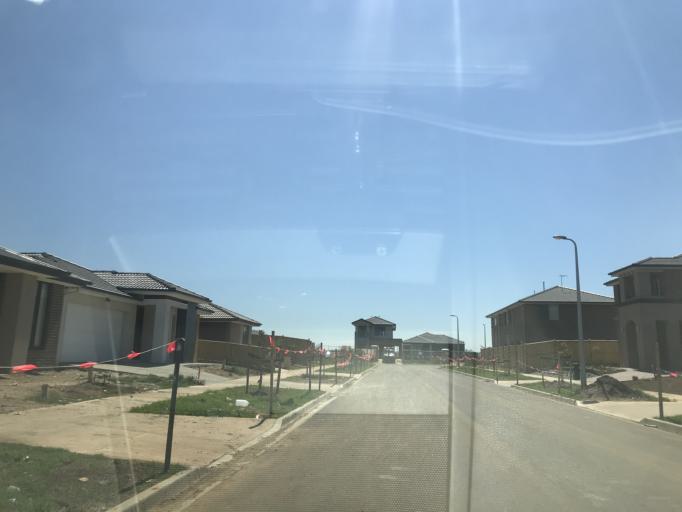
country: AU
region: Victoria
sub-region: Wyndham
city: Truganina
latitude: -37.8351
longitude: 144.7241
